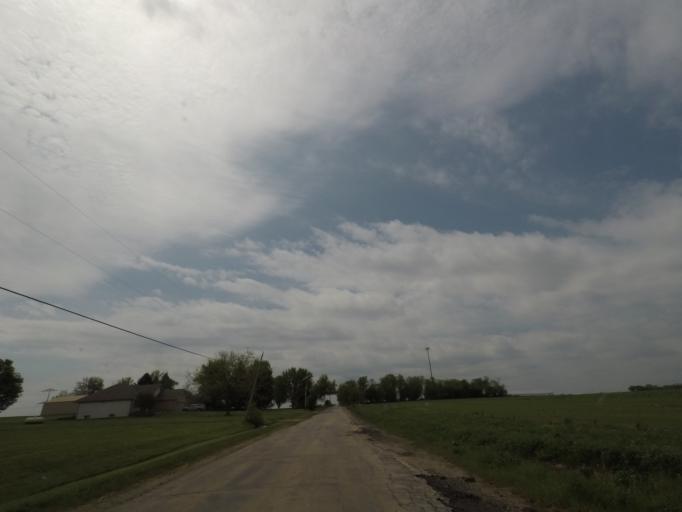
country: US
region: Illinois
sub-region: Winnebago County
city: Machesney Park
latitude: 42.3425
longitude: -88.9493
